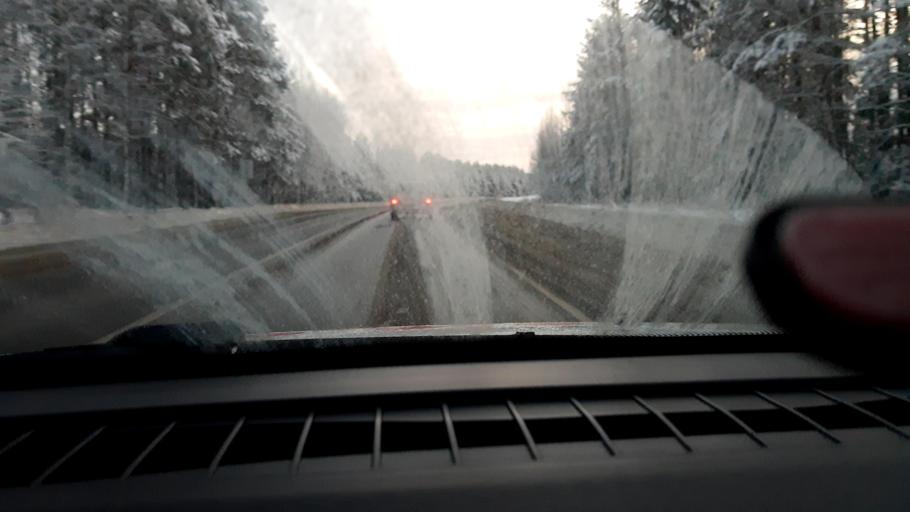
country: RU
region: Nizjnij Novgorod
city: Krasnyye Baki
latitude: 56.9872
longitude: 45.1180
